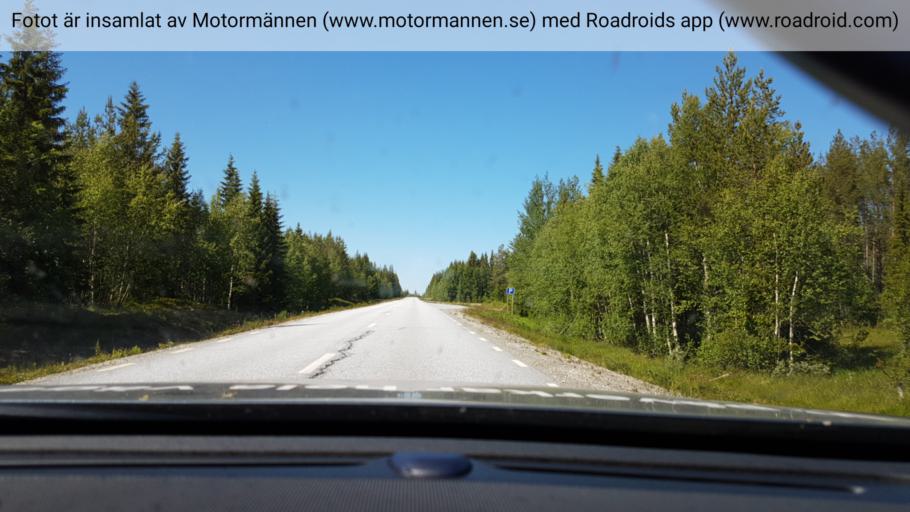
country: SE
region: Vaesterbotten
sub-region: Vilhelmina Kommun
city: Sjoberg
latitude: 64.8045
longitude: 15.9970
